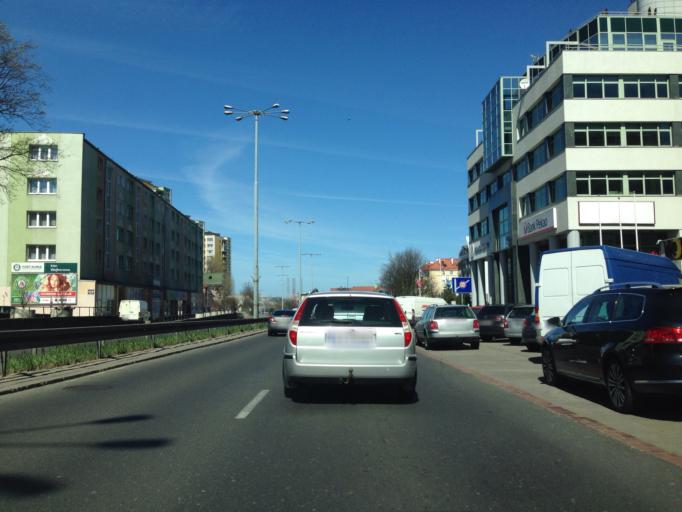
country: PL
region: Pomeranian Voivodeship
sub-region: Gdynia
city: Gdynia
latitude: 54.5156
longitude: 18.5323
